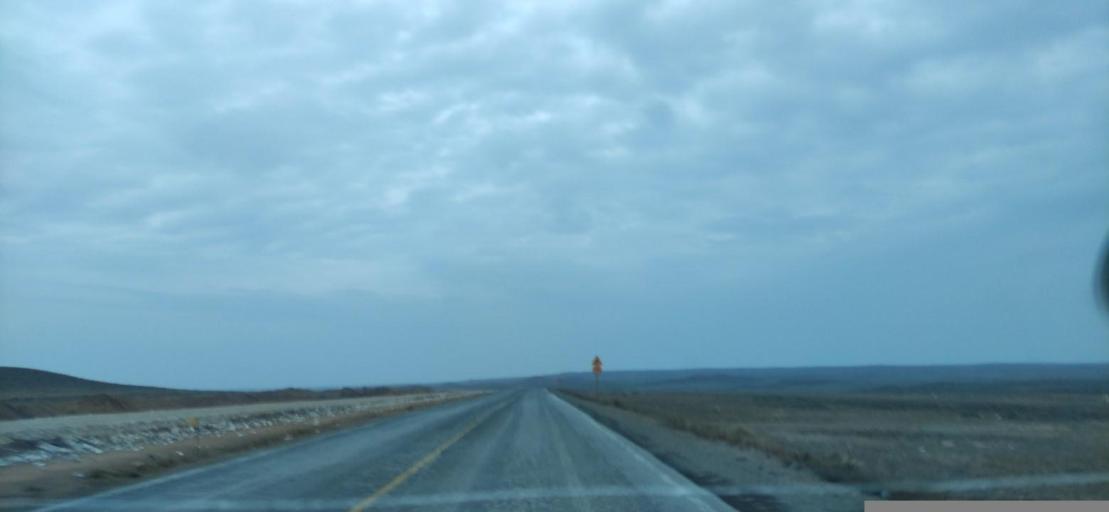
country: KZ
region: Qaraghandy
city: Saryshaghan
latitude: 46.3356
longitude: 73.8046
